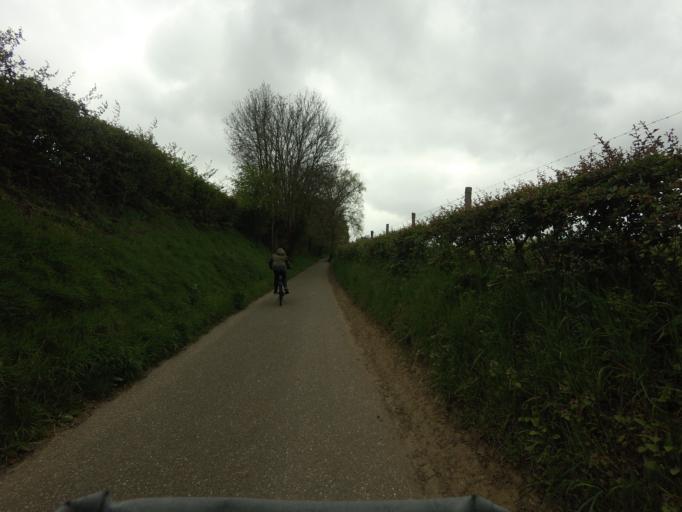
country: NL
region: Limburg
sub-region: Gemeente Schinnen
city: Puth
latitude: 50.9379
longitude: 5.8573
